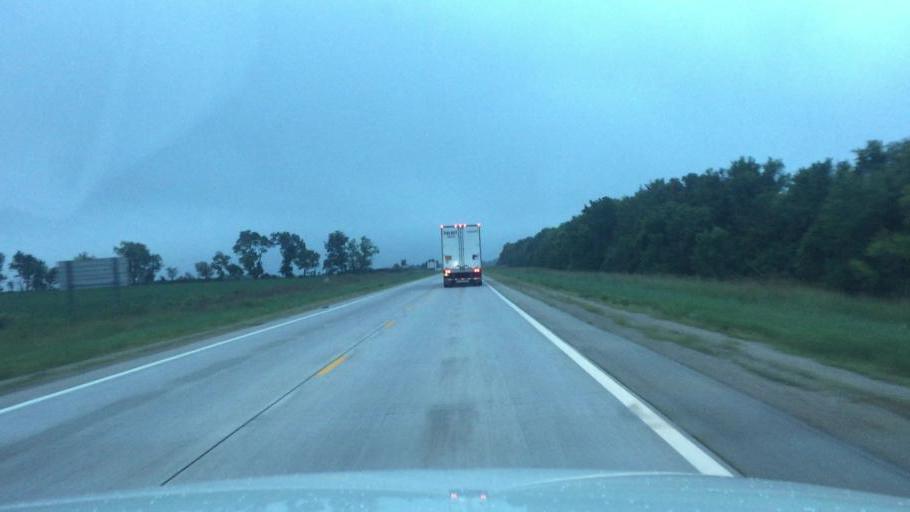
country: US
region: Kansas
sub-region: Neosho County
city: Chanute
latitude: 37.6367
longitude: -95.4796
